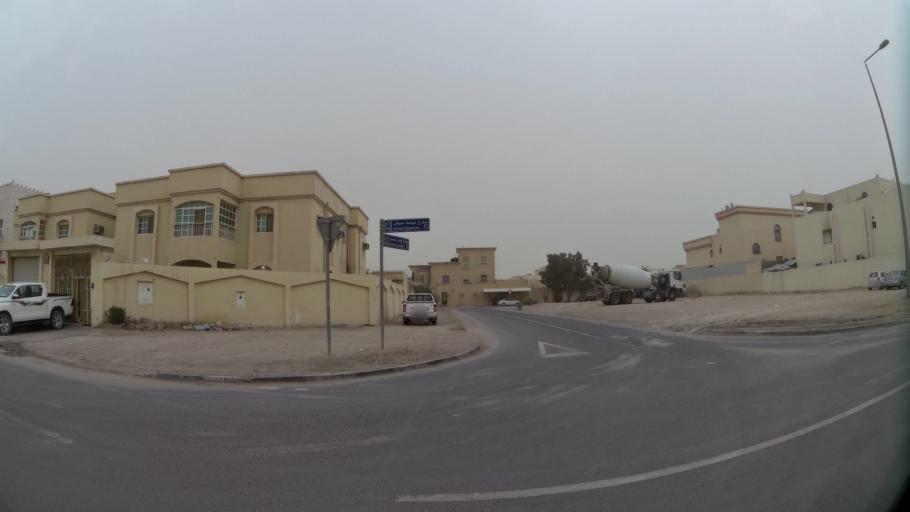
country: QA
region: Baladiyat ad Dawhah
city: Doha
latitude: 25.2394
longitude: 51.4890
